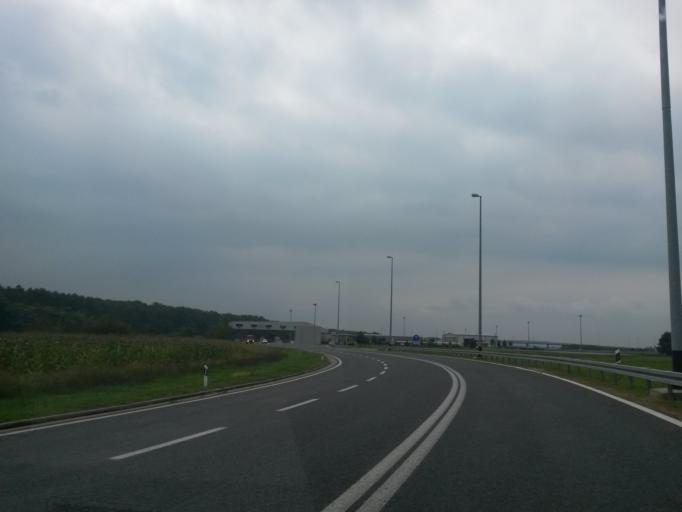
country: HR
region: Osjecko-Baranjska
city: Piskorevci
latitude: 45.3262
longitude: 18.3869
